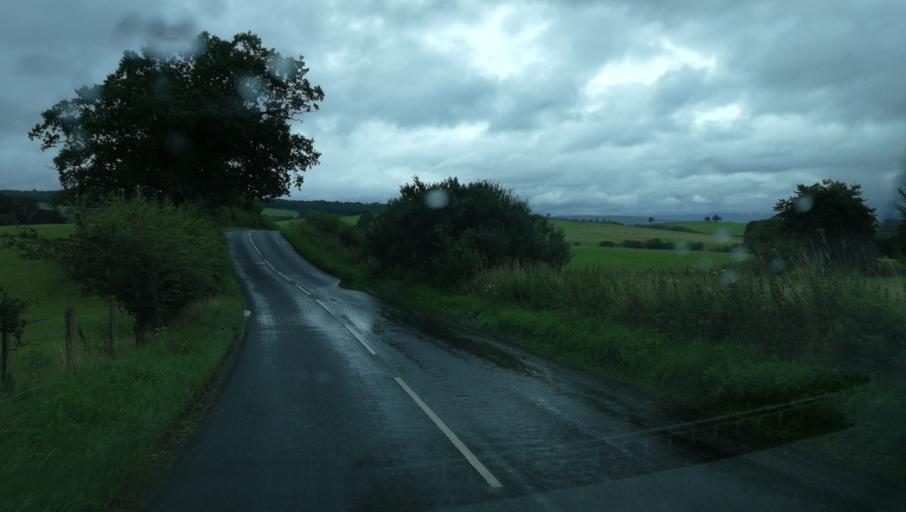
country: GB
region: England
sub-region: Cumbria
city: Penrith
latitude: 54.6208
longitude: -2.8238
